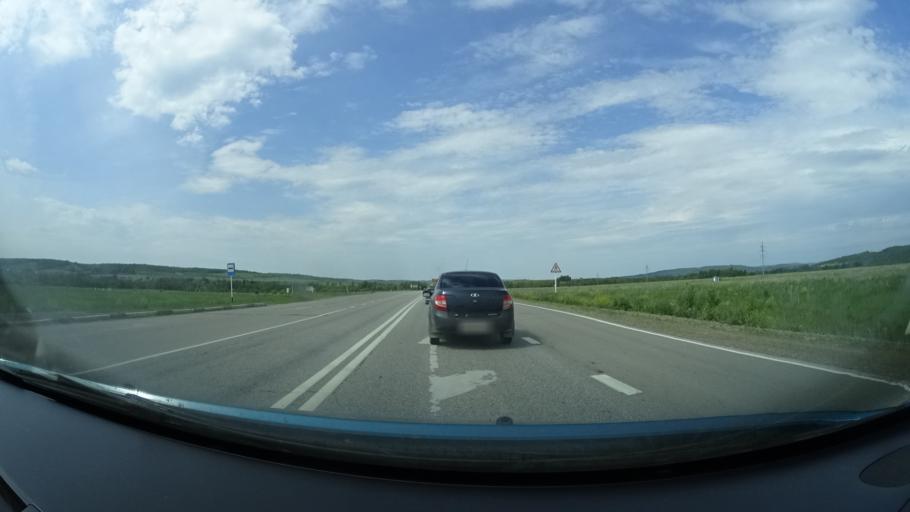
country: RU
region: Perm
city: Barda
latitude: 57.0203
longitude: 55.5563
